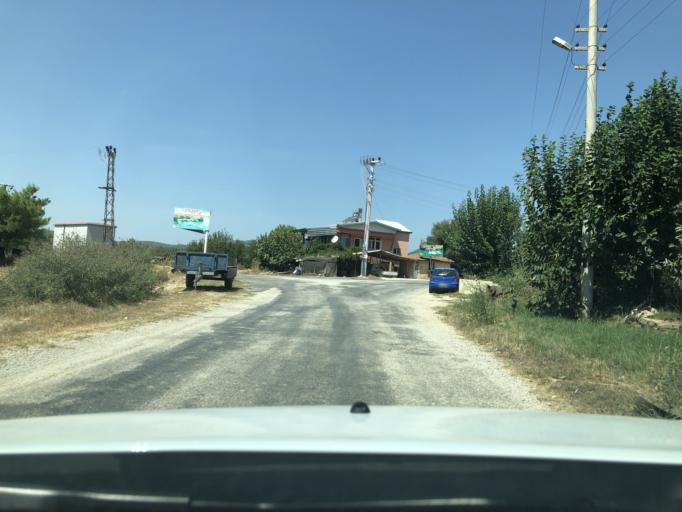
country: TR
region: Antalya
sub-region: Manavgat
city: Kizilagac
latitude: 36.8570
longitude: 31.5634
